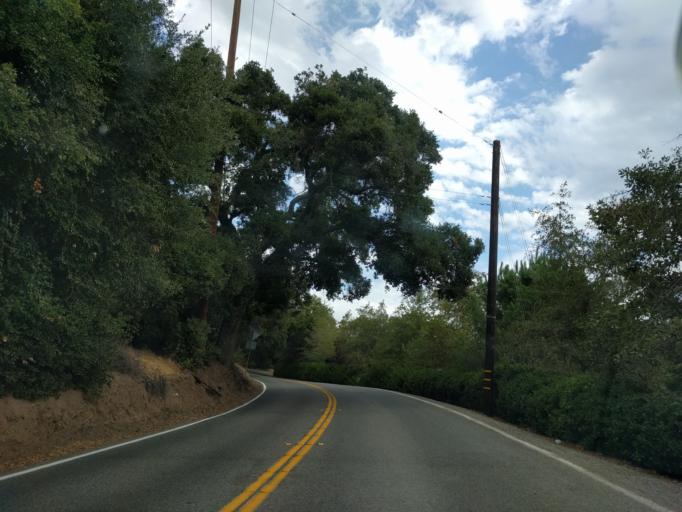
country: US
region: California
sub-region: Orange County
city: Trabuco Canyon
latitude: 33.6548
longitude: -117.6004
